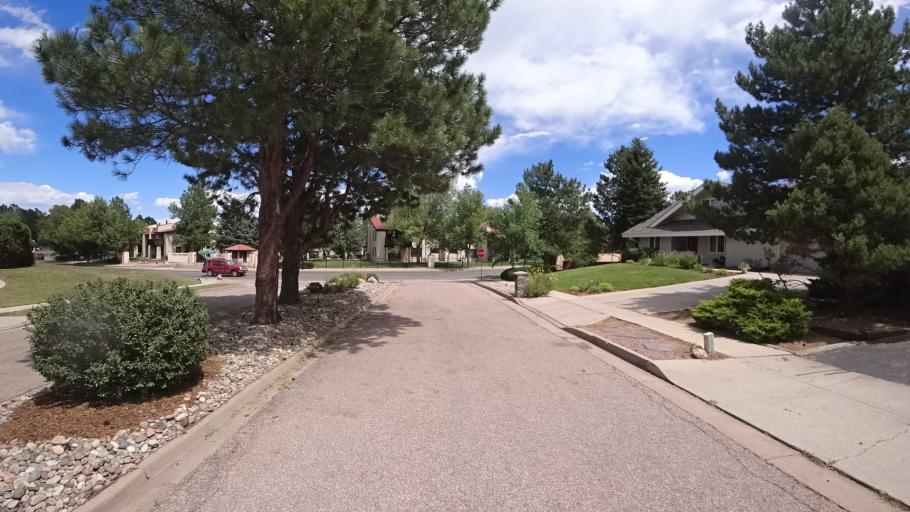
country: US
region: Colorado
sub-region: El Paso County
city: Colorado Springs
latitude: 38.7872
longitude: -104.8252
